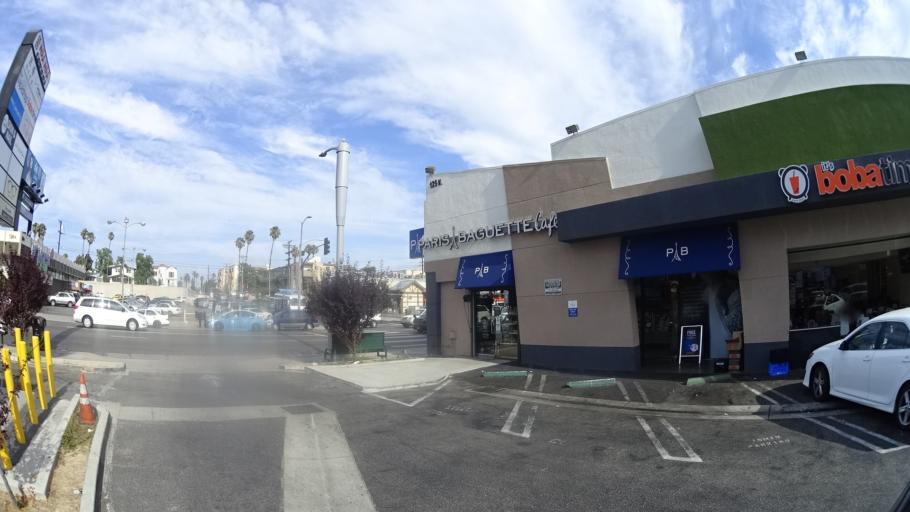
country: US
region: California
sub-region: Los Angeles County
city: Hollywood
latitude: 34.0739
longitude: -118.3094
